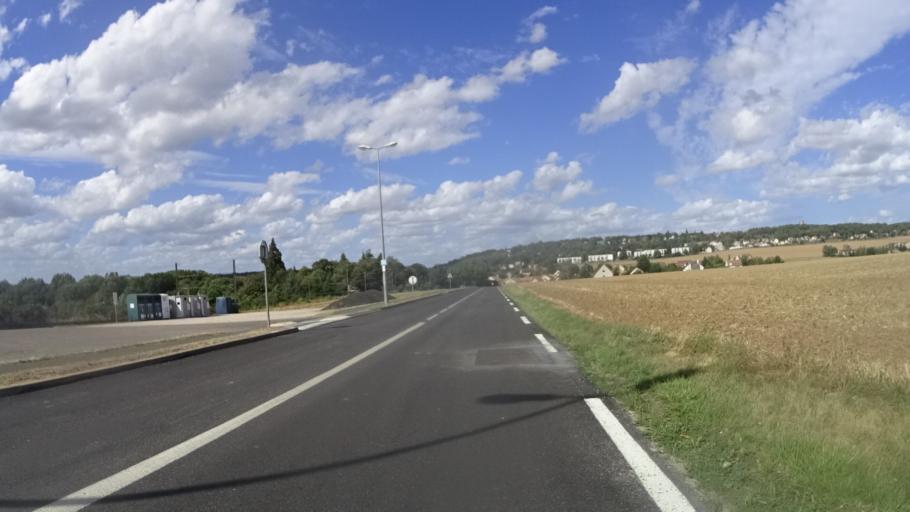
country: FR
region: Ile-de-France
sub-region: Departement de l'Essonne
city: La Ferte-Alais
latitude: 48.4679
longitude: 2.3534
